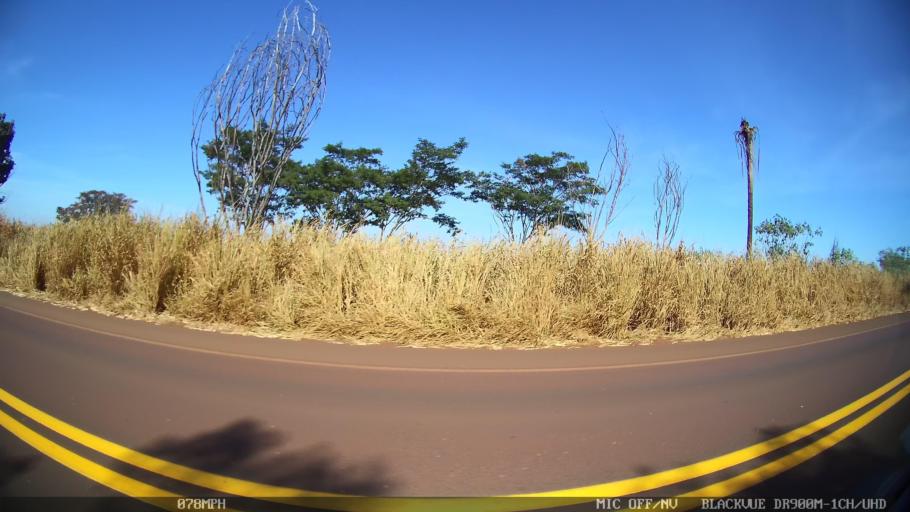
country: BR
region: Sao Paulo
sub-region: Barretos
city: Barretos
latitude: -20.4638
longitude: -48.4724
